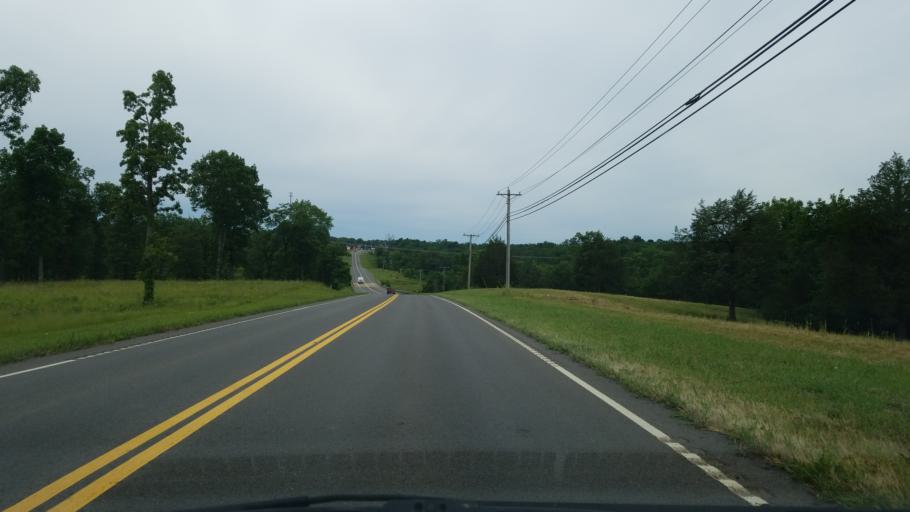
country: US
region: Tennessee
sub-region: Bradley County
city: Hopewell
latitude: 35.3100
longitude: -84.9536
